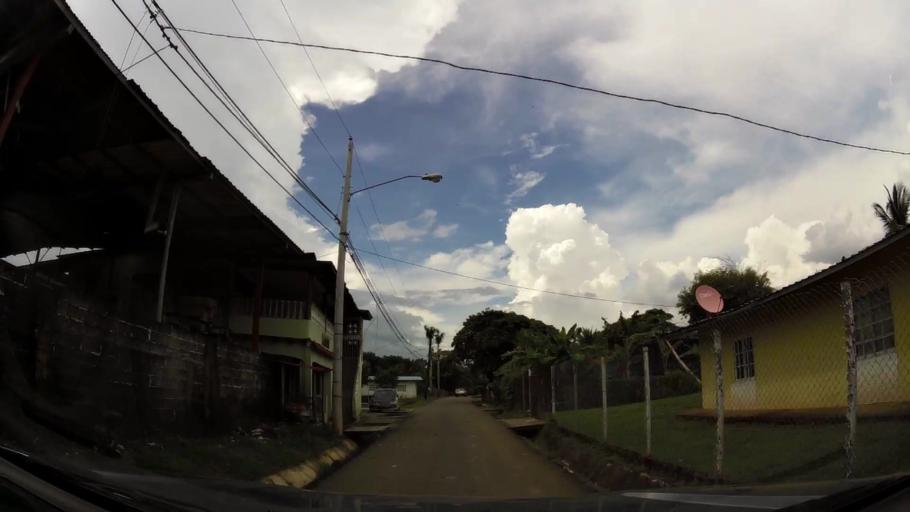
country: PA
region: Panama
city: Cabra Numero Uno
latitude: 9.1110
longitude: -79.3355
